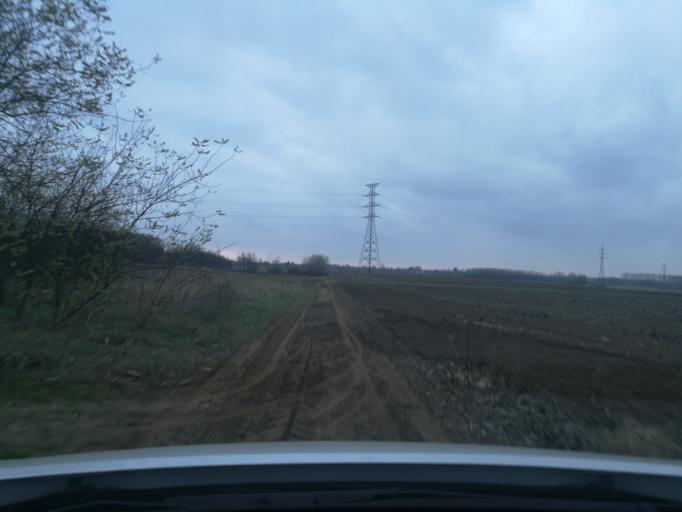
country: HU
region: Szabolcs-Szatmar-Bereg
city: Nyirpazony
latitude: 47.9680
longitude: 21.7852
